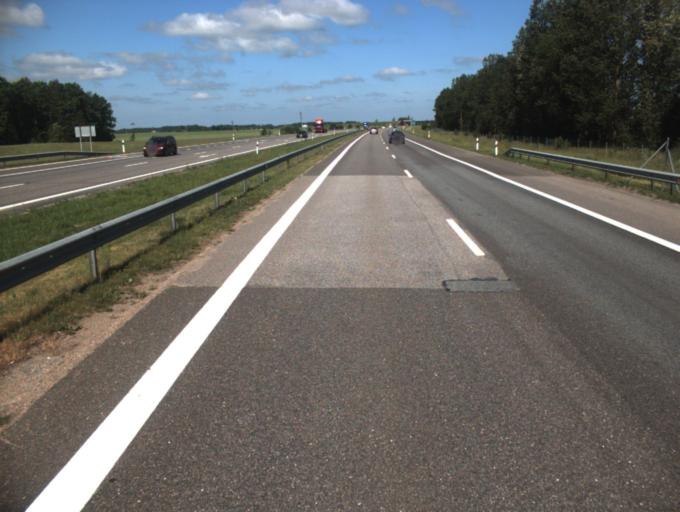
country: LT
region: Klaipedos apskritis
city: Gargzdai
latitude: 55.7118
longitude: 21.4639
